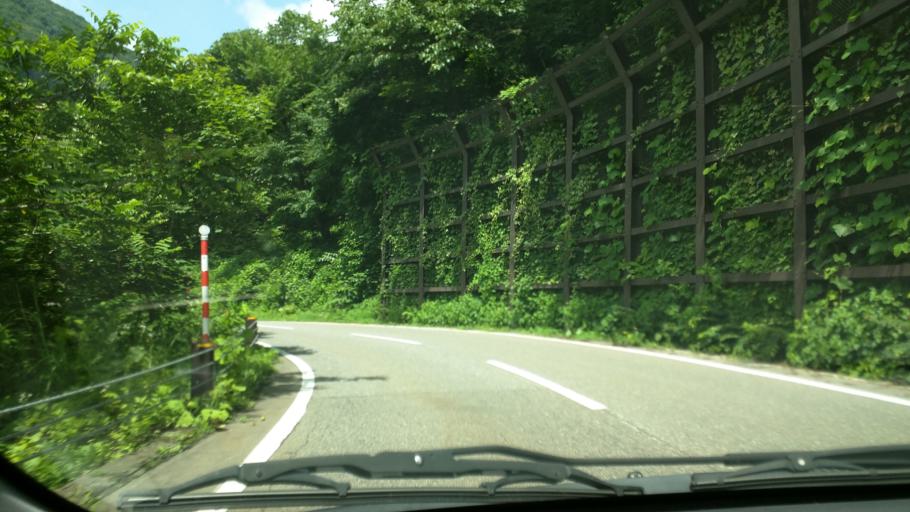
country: JP
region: Fukushima
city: Kitakata
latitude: 37.3088
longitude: 139.8884
